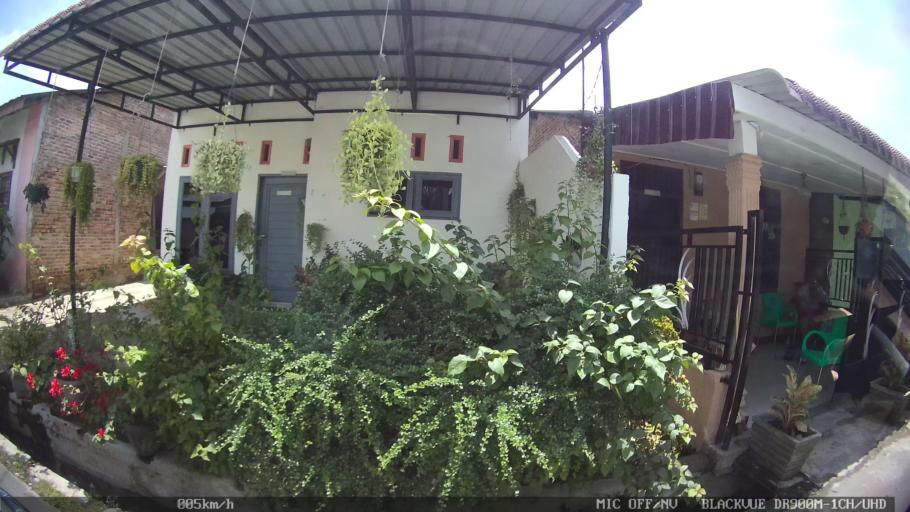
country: ID
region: North Sumatra
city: Percut
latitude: 3.5513
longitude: 98.8515
